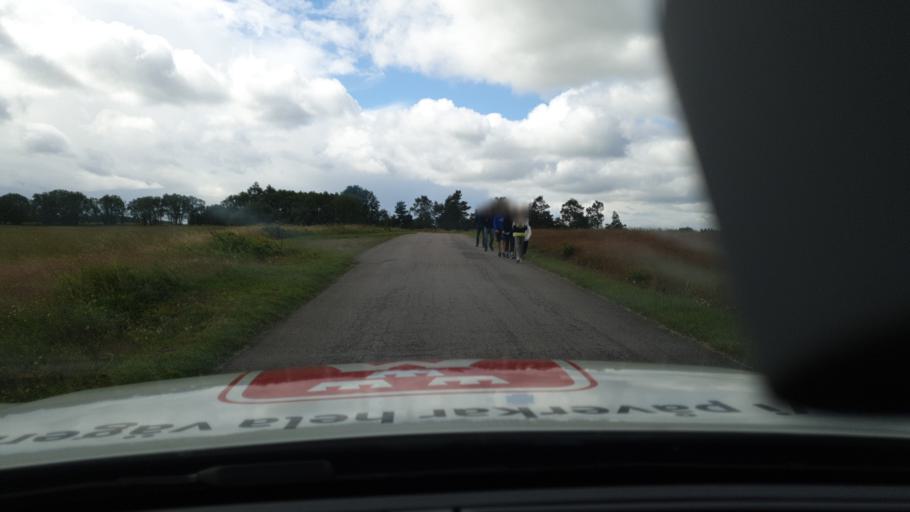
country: SE
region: Vaestra Goetaland
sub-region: Falkopings Kommun
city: Falkoeping
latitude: 58.1357
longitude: 13.6053
